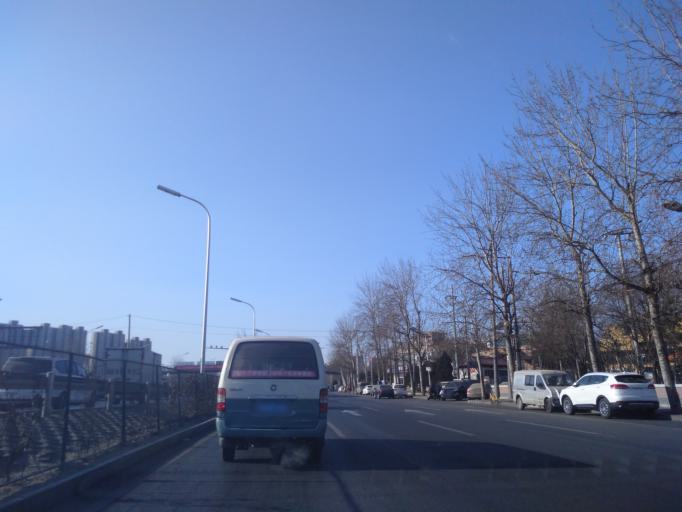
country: CN
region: Beijing
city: Jiugong
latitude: 39.8354
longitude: 116.4634
